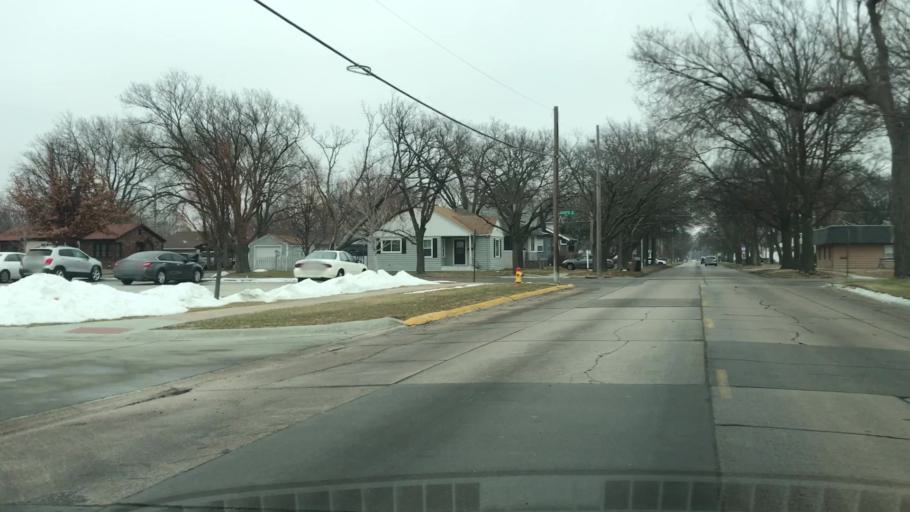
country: US
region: Nebraska
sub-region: Hall County
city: Grand Island
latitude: 40.9385
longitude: -98.3648
